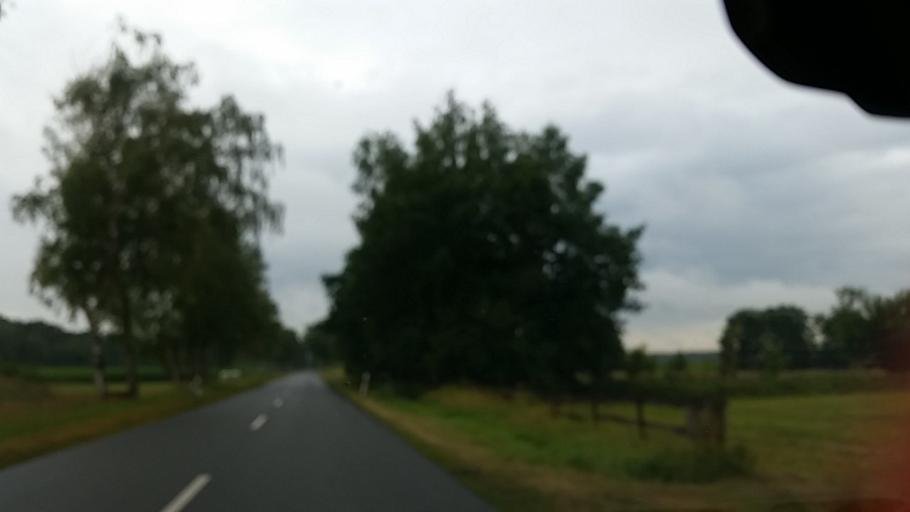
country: DE
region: Lower Saxony
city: Schoneworde
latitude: 52.6600
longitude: 10.6987
